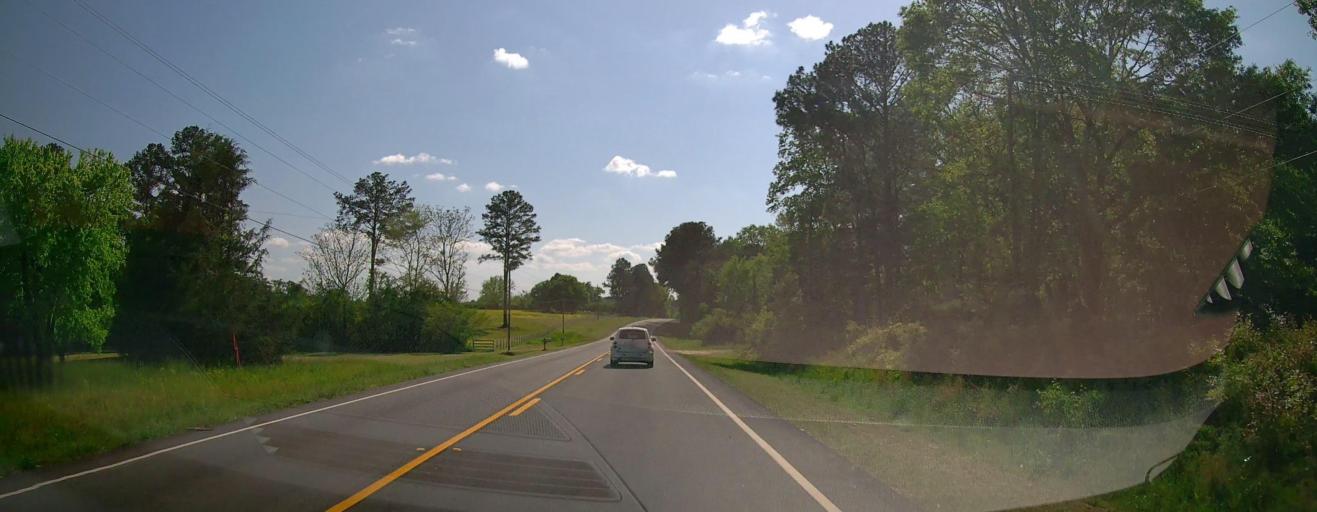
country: US
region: Georgia
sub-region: Morgan County
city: Madison
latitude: 33.6024
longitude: -83.3975
